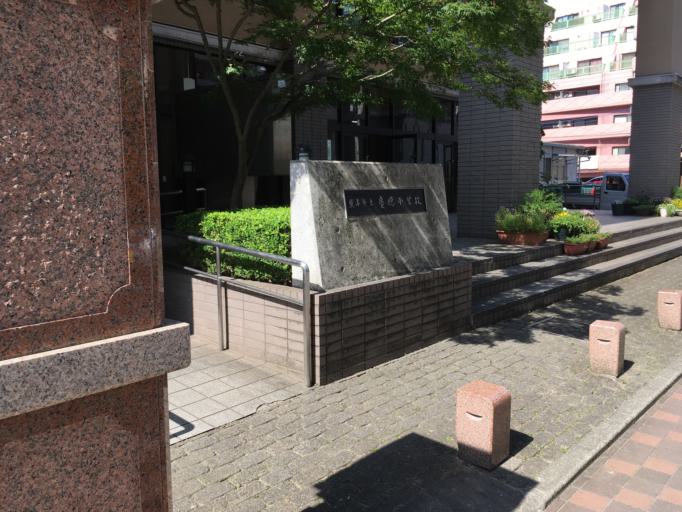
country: JP
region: Kumamoto
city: Kumamoto
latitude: 32.7975
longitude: 130.7020
